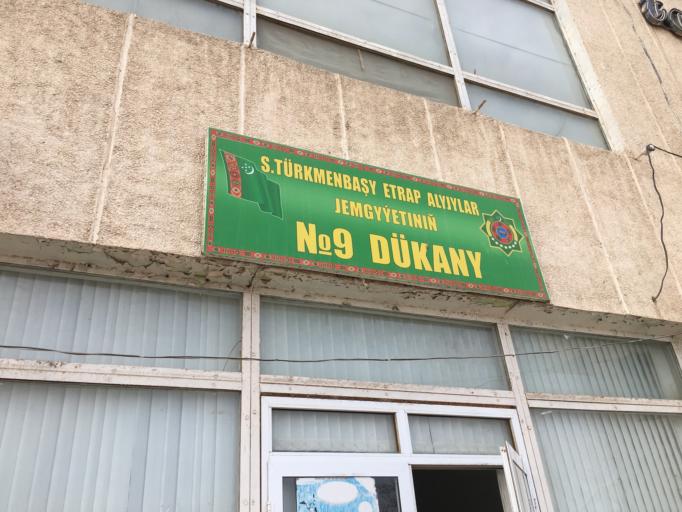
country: UZ
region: Karakalpakstan
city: Shumanay Shahri
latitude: 42.3781
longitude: 58.8088
